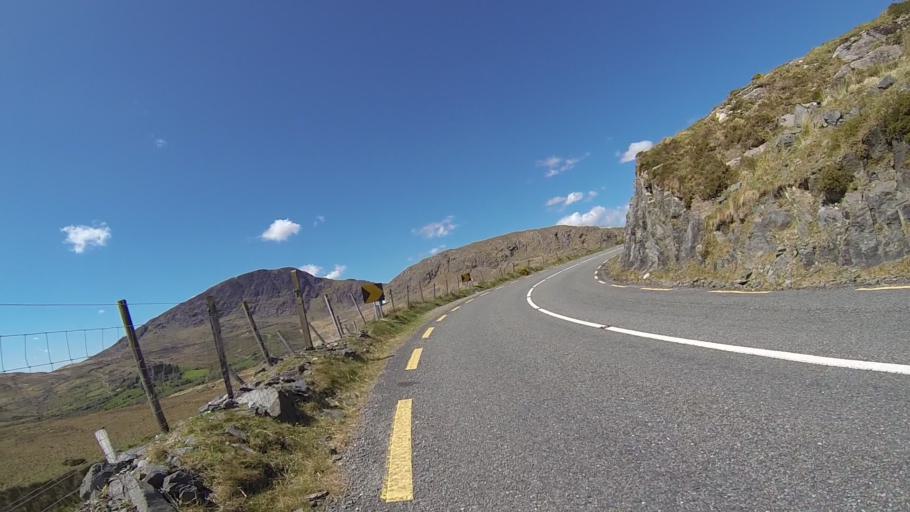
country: IE
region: Munster
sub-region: Ciarrai
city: Kenmare
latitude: 51.9275
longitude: -9.6448
